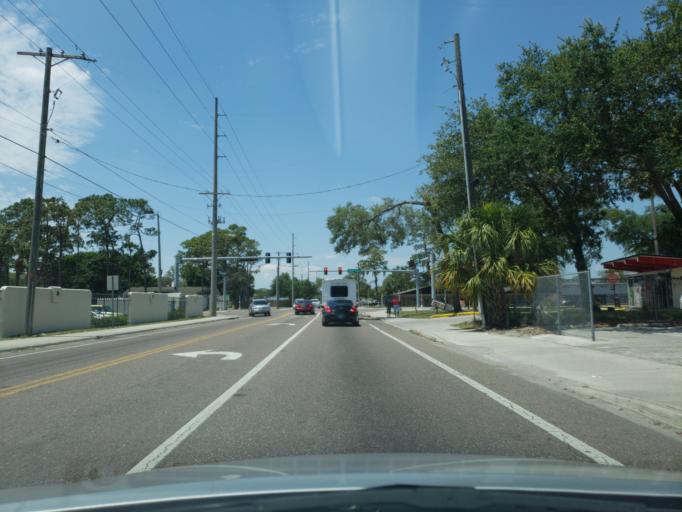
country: US
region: Florida
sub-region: Hillsborough County
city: University
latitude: 28.0656
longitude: -82.4338
